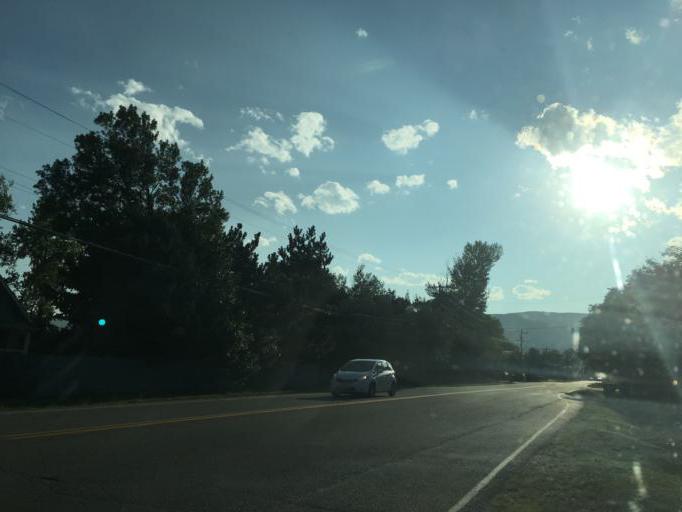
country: US
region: Colorado
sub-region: Jefferson County
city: Applewood
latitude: 39.7908
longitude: -105.1695
